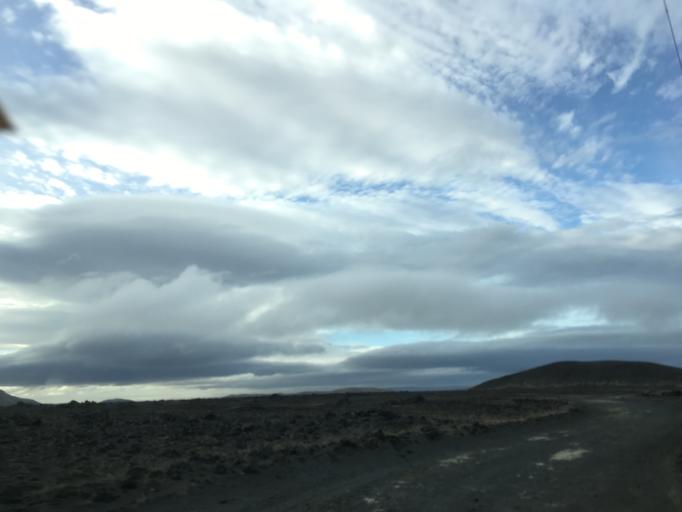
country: IS
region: South
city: Vestmannaeyjar
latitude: 64.1204
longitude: -19.1165
